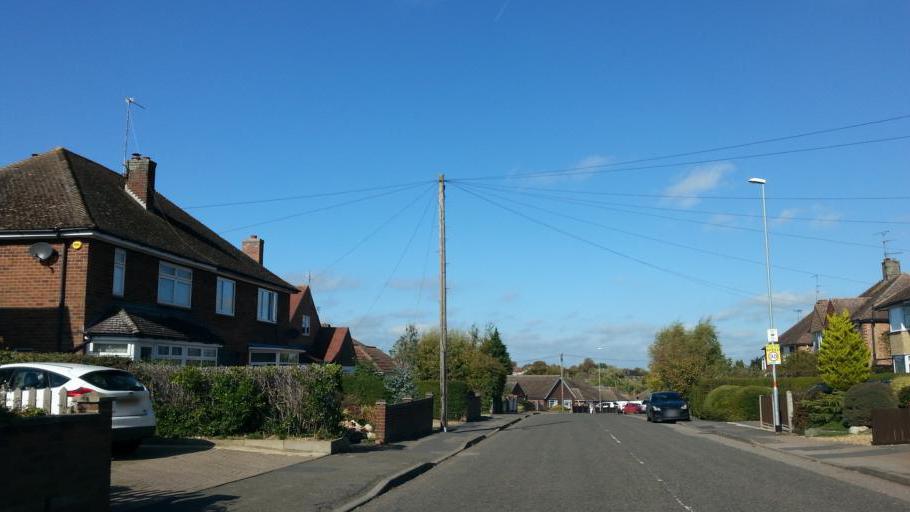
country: GB
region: England
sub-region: Northamptonshire
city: Rushden
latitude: 52.2844
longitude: -0.6033
